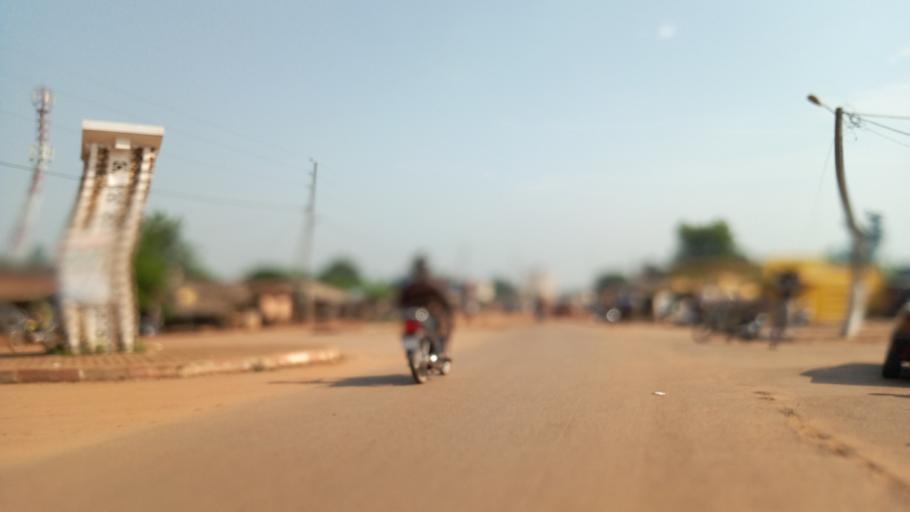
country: BJ
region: Queme
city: Porto-Novo
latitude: 6.5543
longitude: 2.6567
